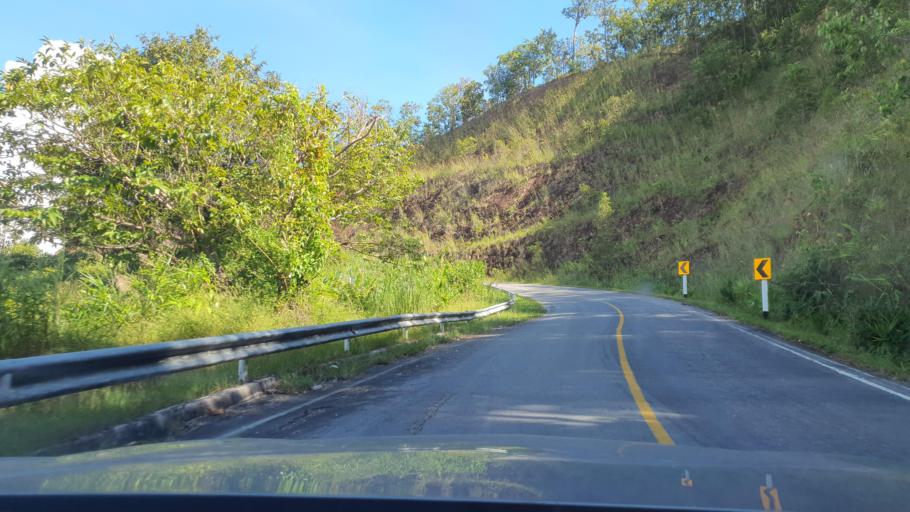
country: TH
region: Chiang Mai
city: Phrao
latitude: 19.3616
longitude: 99.2733
